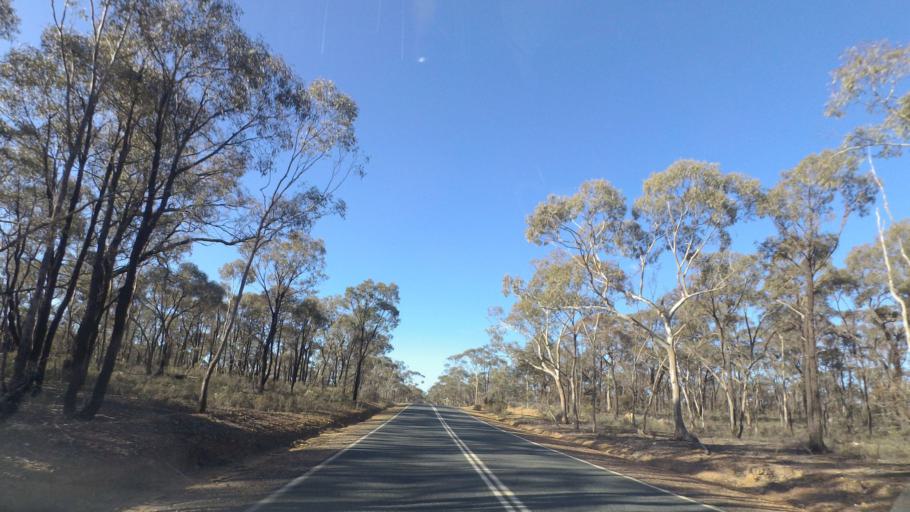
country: AU
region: Victoria
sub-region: Greater Bendigo
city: Epsom
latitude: -36.6679
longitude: 144.4284
